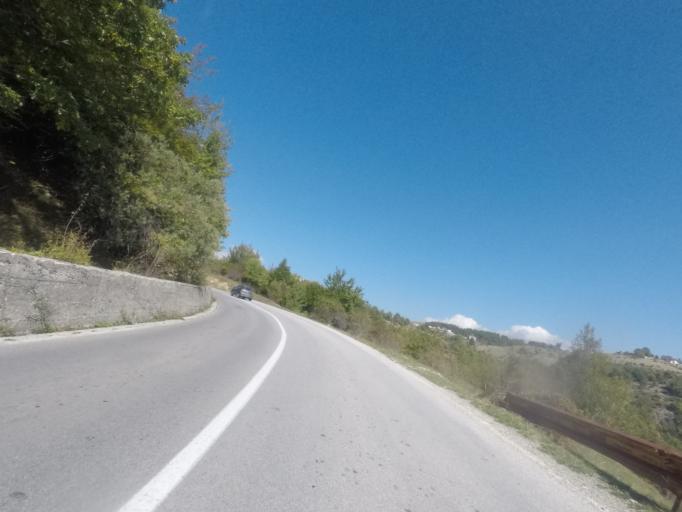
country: ME
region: Opstina Pluzine
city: Pluzine
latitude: 43.1131
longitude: 18.8225
